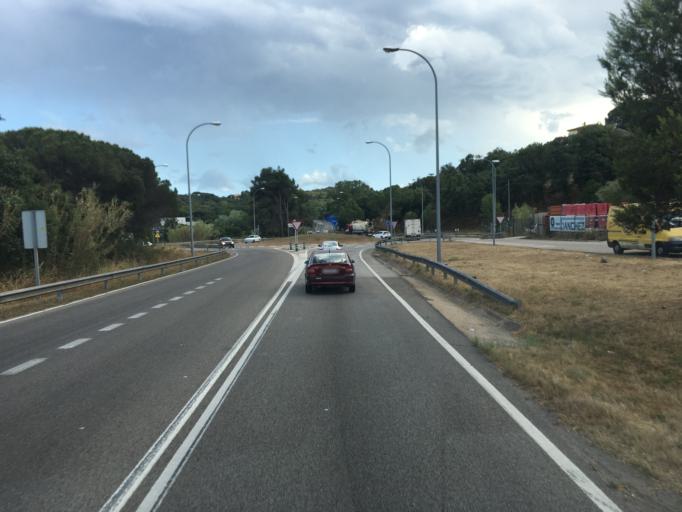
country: ES
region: Catalonia
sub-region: Provincia de Barcelona
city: Tordera
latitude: 41.6848
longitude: 2.7217
